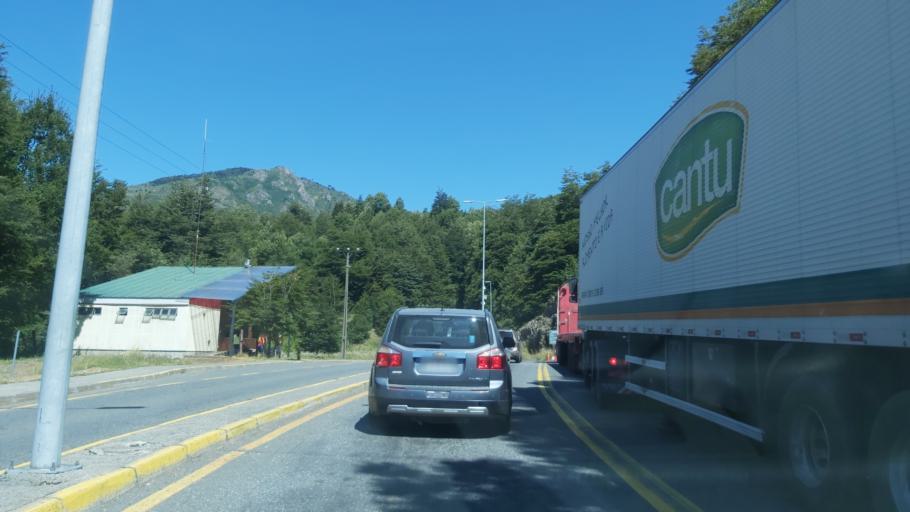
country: CL
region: Araucania
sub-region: Provincia de Cautin
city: Vilcun
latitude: -38.5163
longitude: -71.5170
